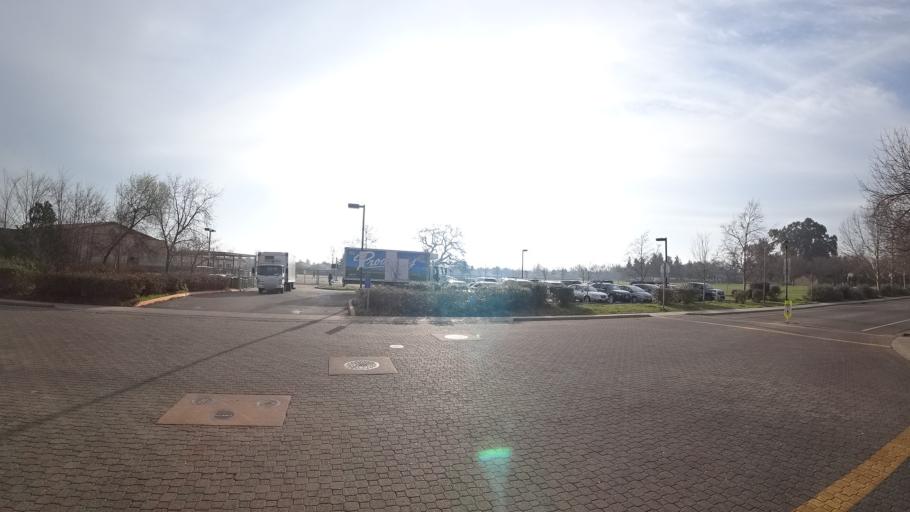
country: US
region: California
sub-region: Yolo County
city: Davis
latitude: 38.5585
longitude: -121.7105
